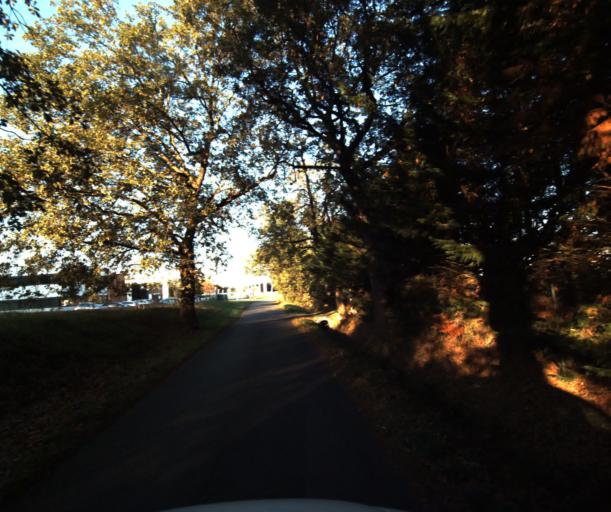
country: FR
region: Midi-Pyrenees
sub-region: Departement de la Haute-Garonne
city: Colomiers
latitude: 43.6293
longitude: 1.3434
